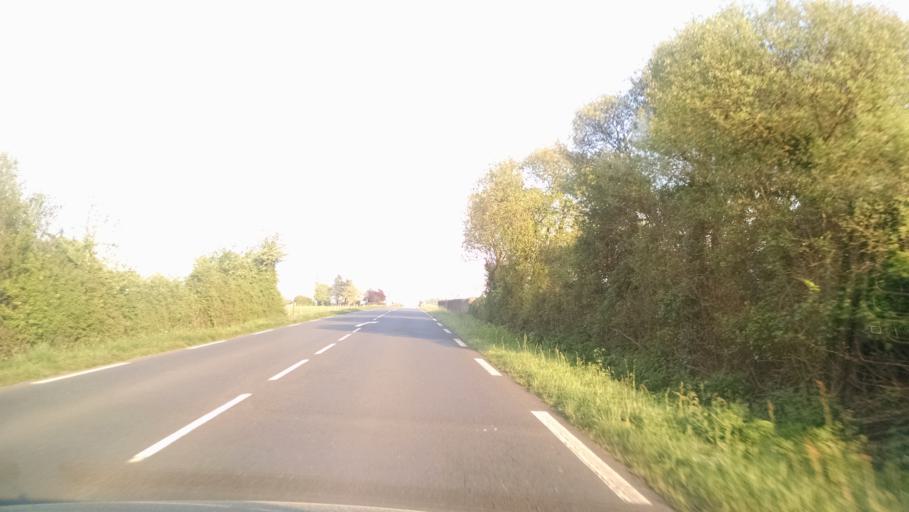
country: FR
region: Pays de la Loire
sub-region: Departement de la Loire-Atlantique
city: Boussay
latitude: 47.0647
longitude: -1.1990
